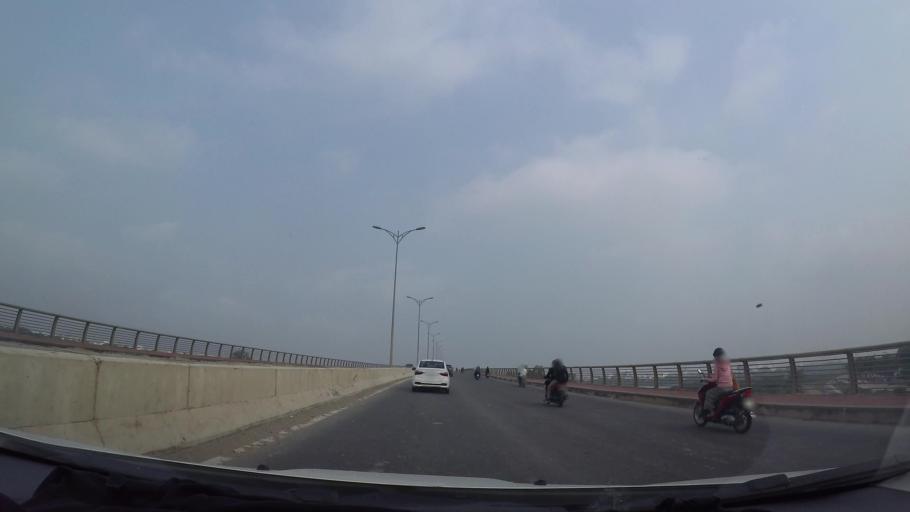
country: VN
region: Da Nang
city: Cam Le
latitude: 16.0126
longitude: 108.2159
